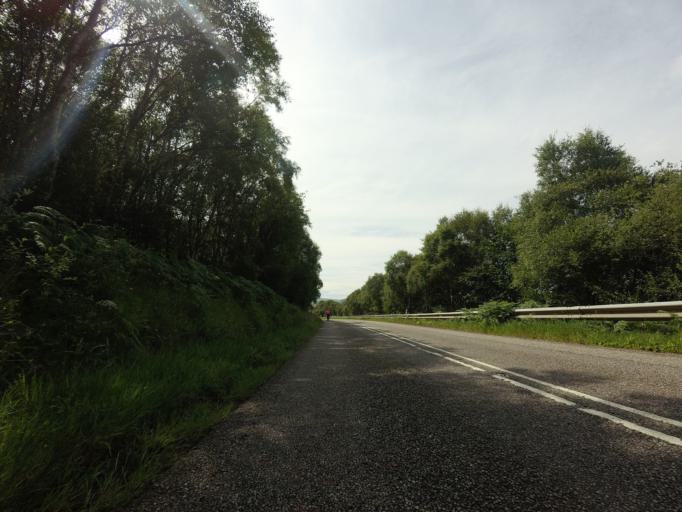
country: GB
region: Scotland
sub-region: Highland
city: Alness
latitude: 57.8553
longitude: -4.2545
